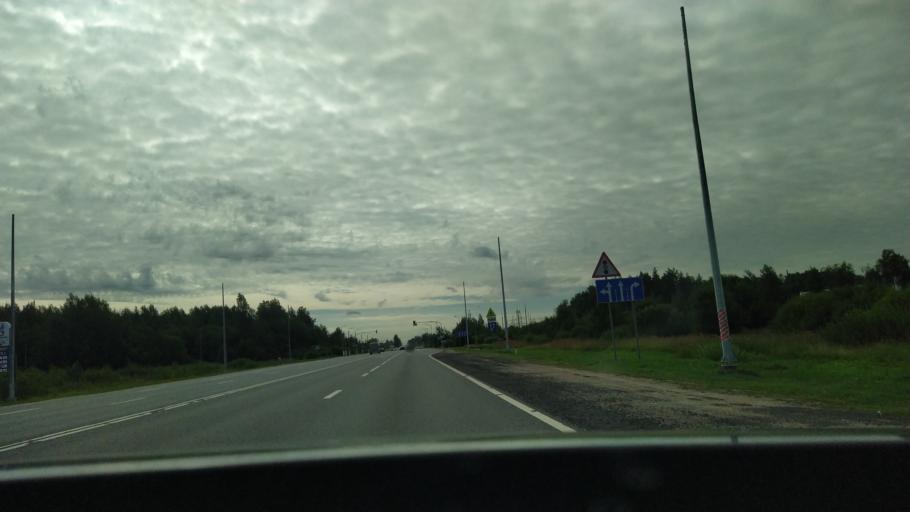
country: RU
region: Leningrad
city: Tosno
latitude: 59.5697
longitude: 30.8245
